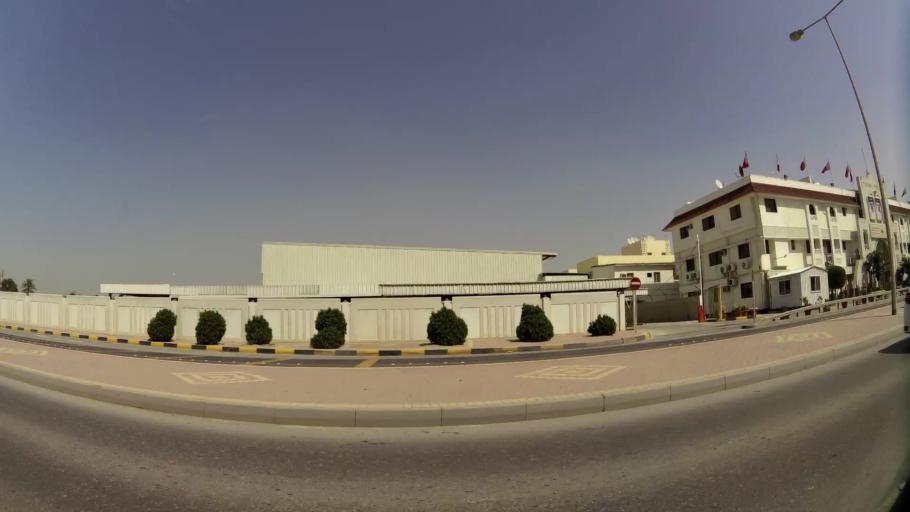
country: BH
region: Manama
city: Jidd Hafs
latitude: 26.2000
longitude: 50.4600
